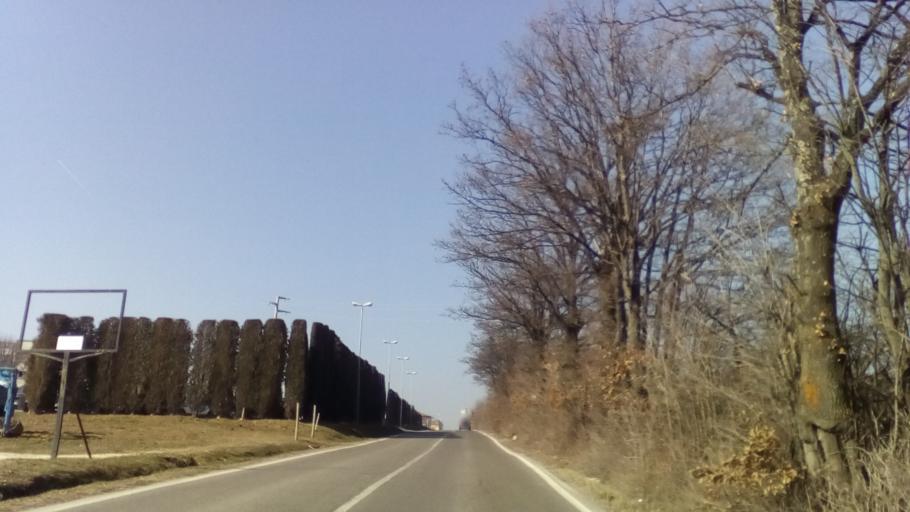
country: IT
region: Emilia-Romagna
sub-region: Provincia di Modena
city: Sant'Antonio
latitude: 44.3781
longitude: 10.8241
